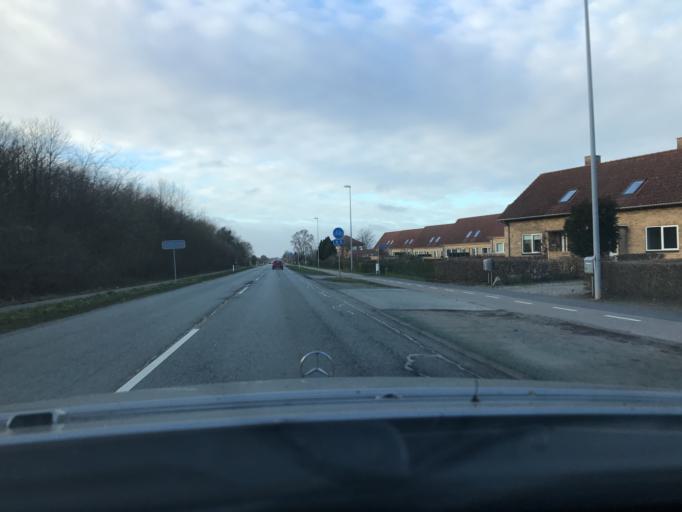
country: DK
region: South Denmark
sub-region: Sonderborg Kommune
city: Nordborg
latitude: 55.0445
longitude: 9.7887
